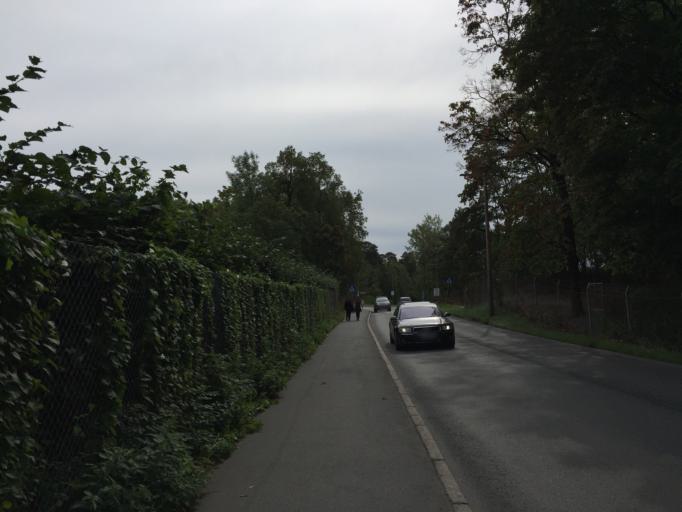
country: NO
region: Oslo
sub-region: Oslo
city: Sjolyststranda
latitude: 59.9103
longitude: 10.6802
